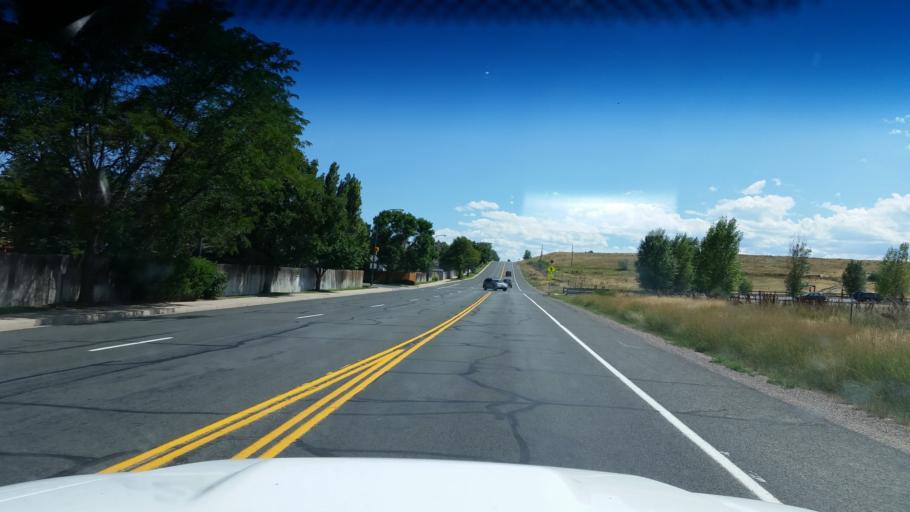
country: US
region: Colorado
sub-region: Broomfield County
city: Broomfield
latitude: 39.8891
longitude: -105.1289
